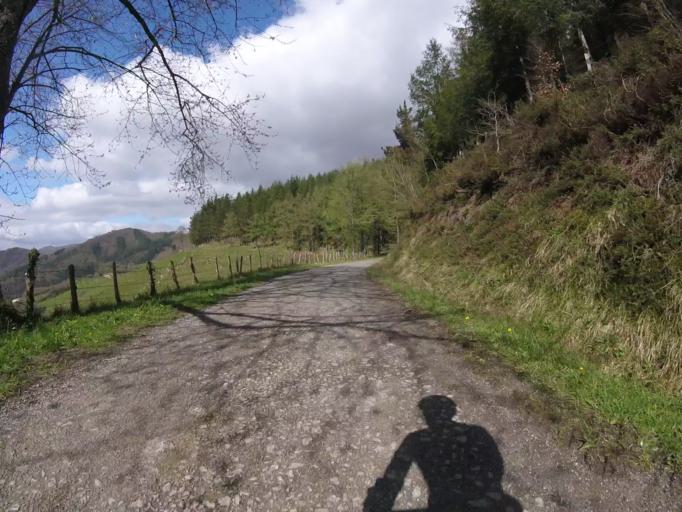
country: ES
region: Basque Country
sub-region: Provincia de Guipuzcoa
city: Albiztur
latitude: 43.1402
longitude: -2.1186
